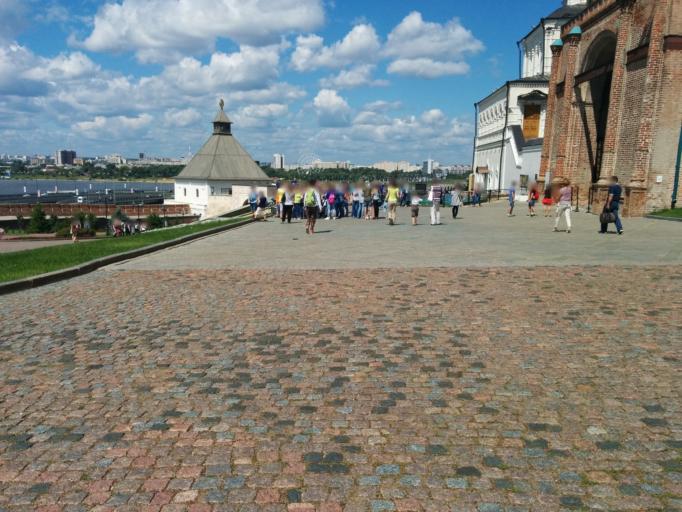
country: RU
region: Tatarstan
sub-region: Gorod Kazan'
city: Kazan
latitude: 55.8001
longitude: 49.1050
